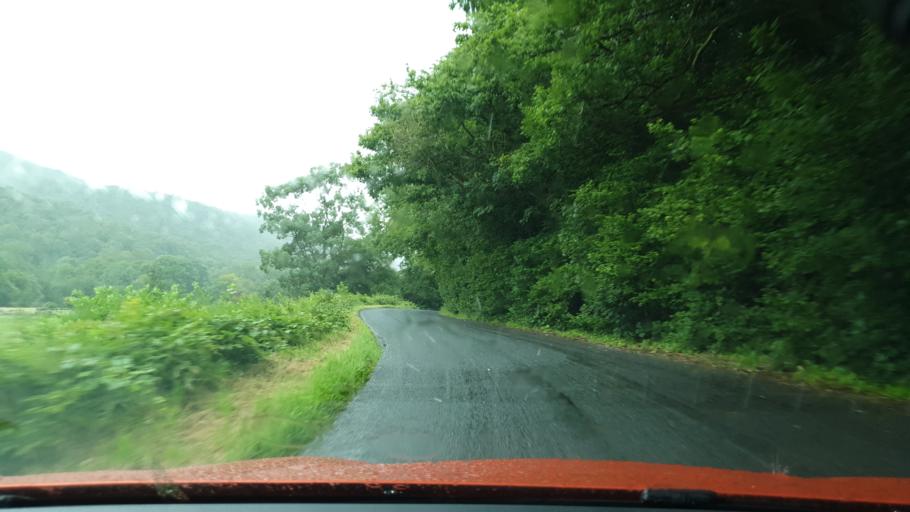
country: GB
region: England
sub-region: Cumbria
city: Millom
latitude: 54.2846
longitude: -3.2315
